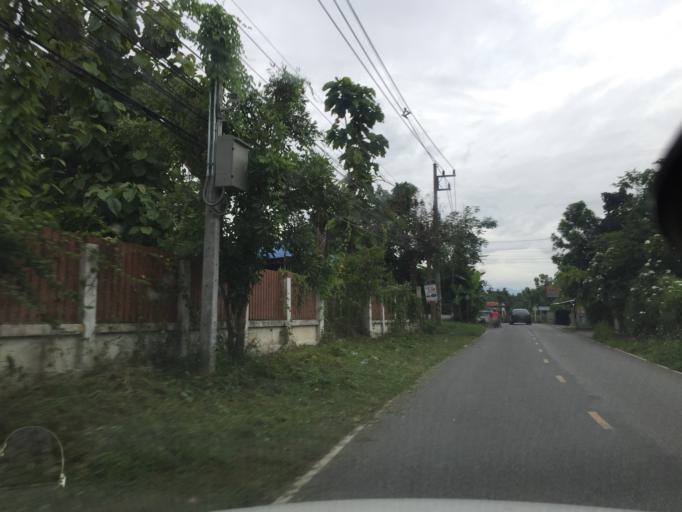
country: TH
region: Chiang Mai
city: Mae On
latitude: 18.8336
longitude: 99.1704
